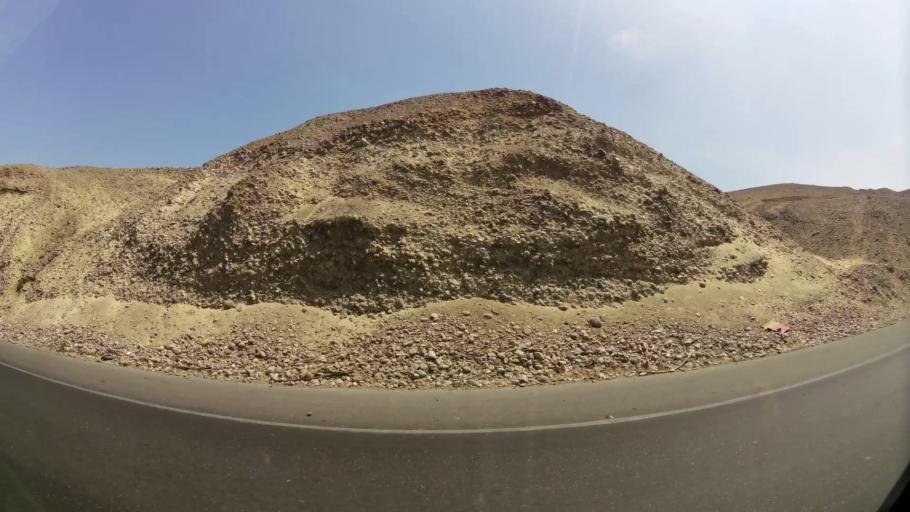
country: PE
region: La Libertad
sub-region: Provincia de Pacasmayo
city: Pacasmayo
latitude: -7.3945
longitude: -79.5571
